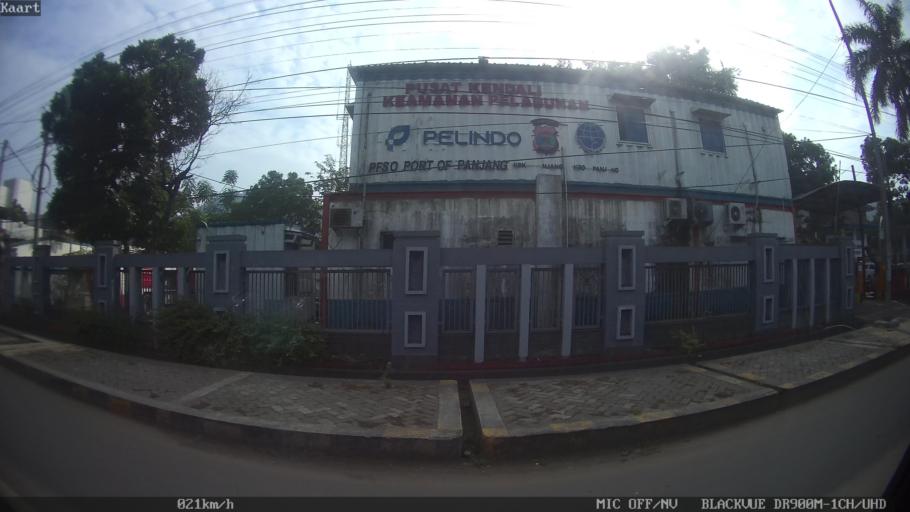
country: ID
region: Lampung
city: Panjang
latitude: -5.4661
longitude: 105.3199
